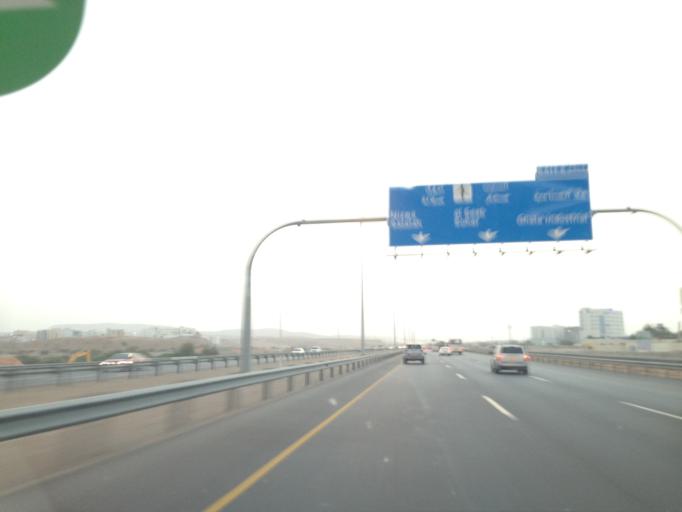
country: OM
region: Muhafazat Masqat
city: Bawshar
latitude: 23.5653
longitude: 58.3587
